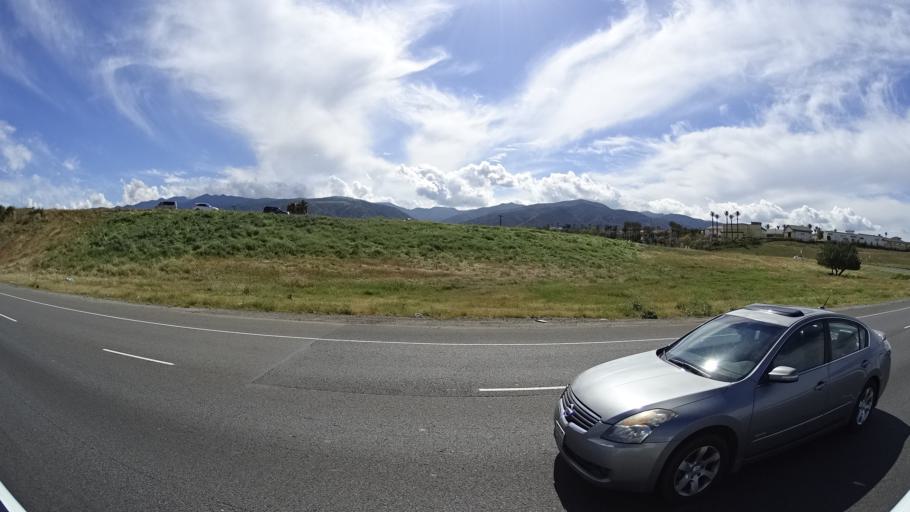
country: US
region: California
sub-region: Riverside County
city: El Cerrito
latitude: 33.8217
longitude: -117.5195
